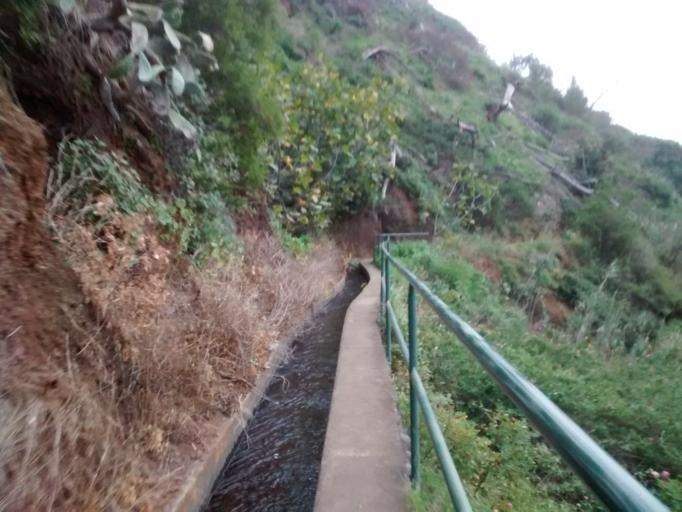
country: PT
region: Madeira
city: Camara de Lobos
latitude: 32.6574
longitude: -16.9611
